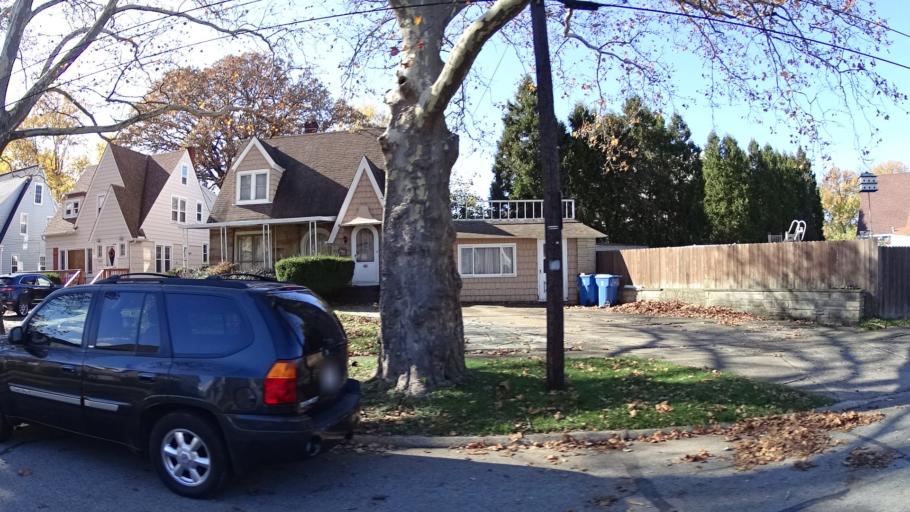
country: US
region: Ohio
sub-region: Lorain County
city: Lorain
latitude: 41.4604
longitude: -82.1971
